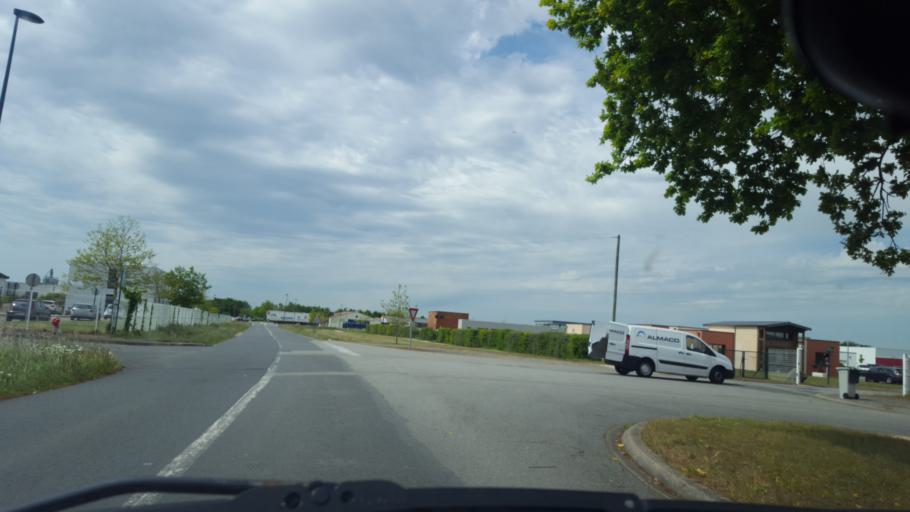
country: FR
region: Pays de la Loire
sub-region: Departement de la Loire-Atlantique
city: Machecoul
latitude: 46.9778
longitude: -1.8015
